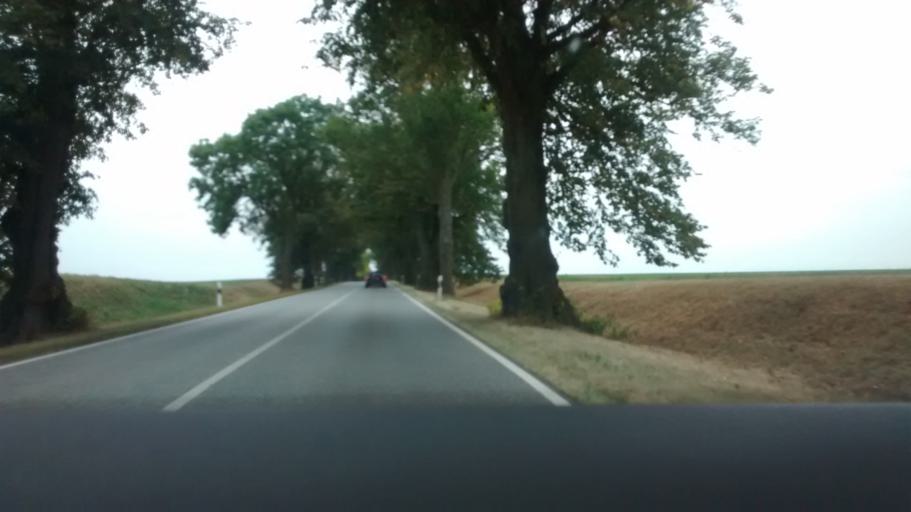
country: DE
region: Mecklenburg-Vorpommern
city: Mecklenburg
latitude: 53.8349
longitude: 11.4569
